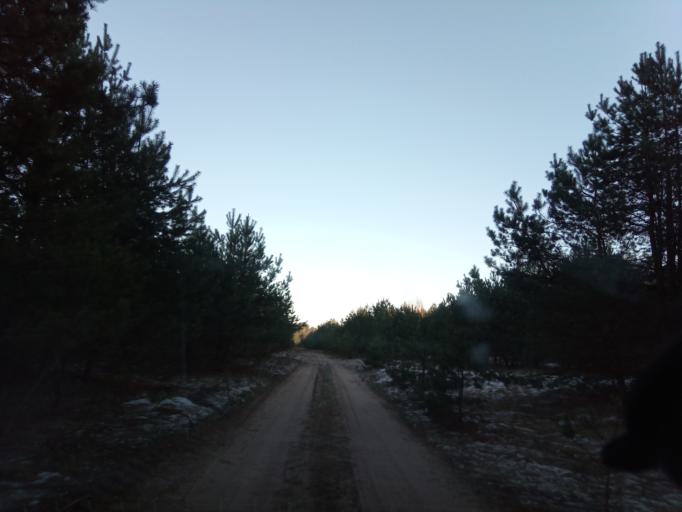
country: LT
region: Alytaus apskritis
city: Druskininkai
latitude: 53.9730
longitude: 23.9549
